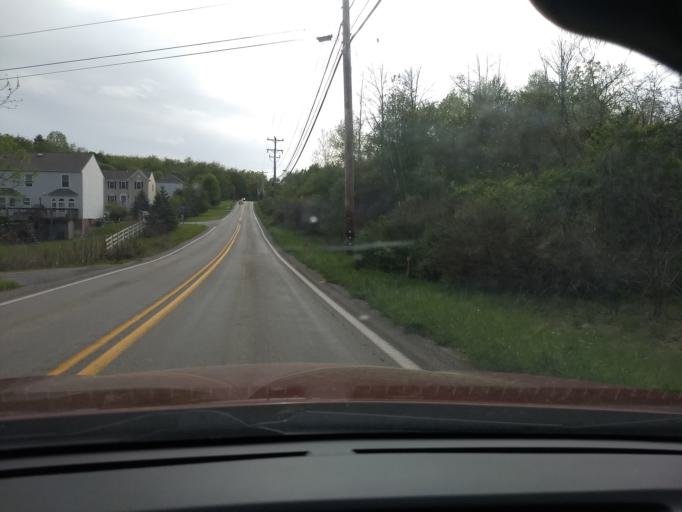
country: US
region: Pennsylvania
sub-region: Allegheny County
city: Bakerstown
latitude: 40.6047
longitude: -79.9233
